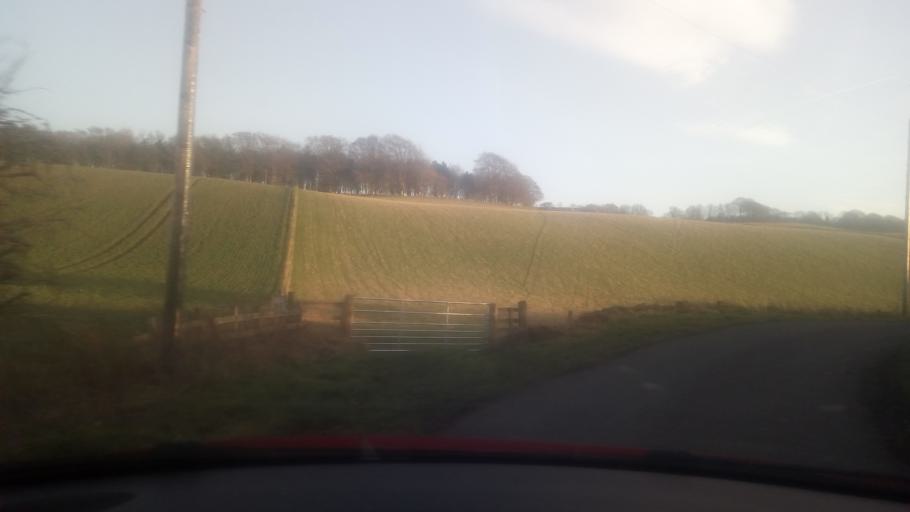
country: GB
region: Scotland
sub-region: The Scottish Borders
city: Jedburgh
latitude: 55.5042
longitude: -2.5364
